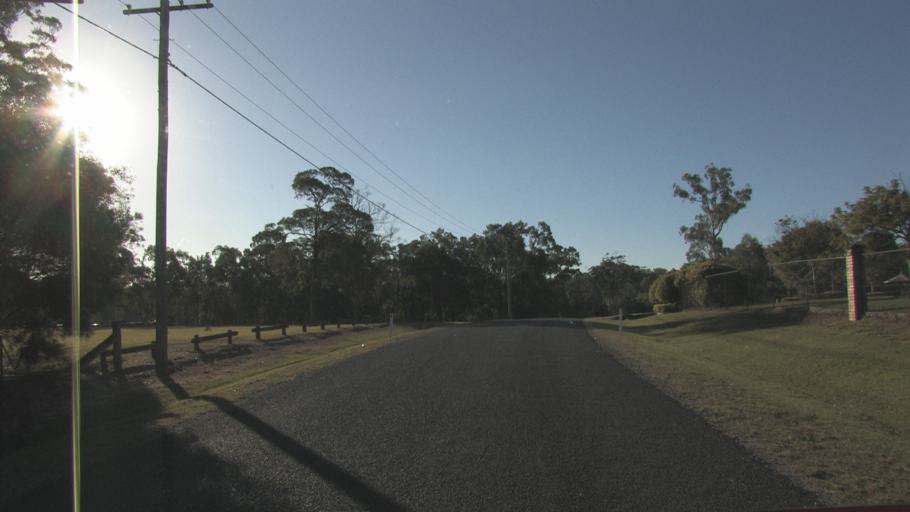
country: AU
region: Queensland
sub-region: Redland
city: Redland Bay
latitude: -27.6621
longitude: 153.2675
